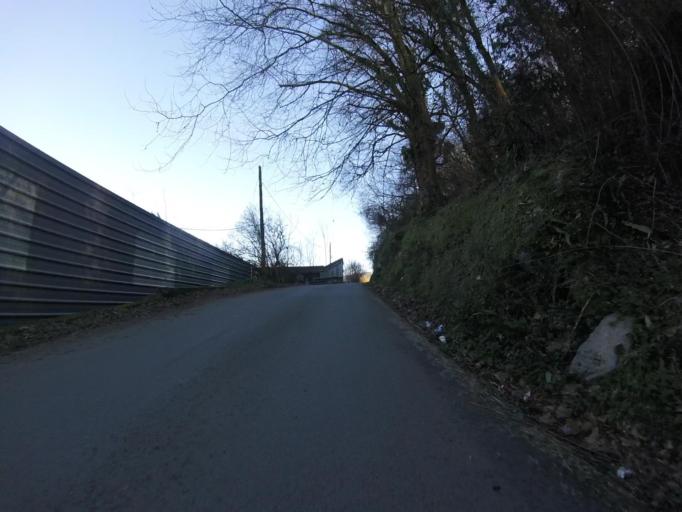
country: ES
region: Basque Country
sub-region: Provincia de Guipuzcoa
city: Errenteria
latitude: 43.2919
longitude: -1.8795
